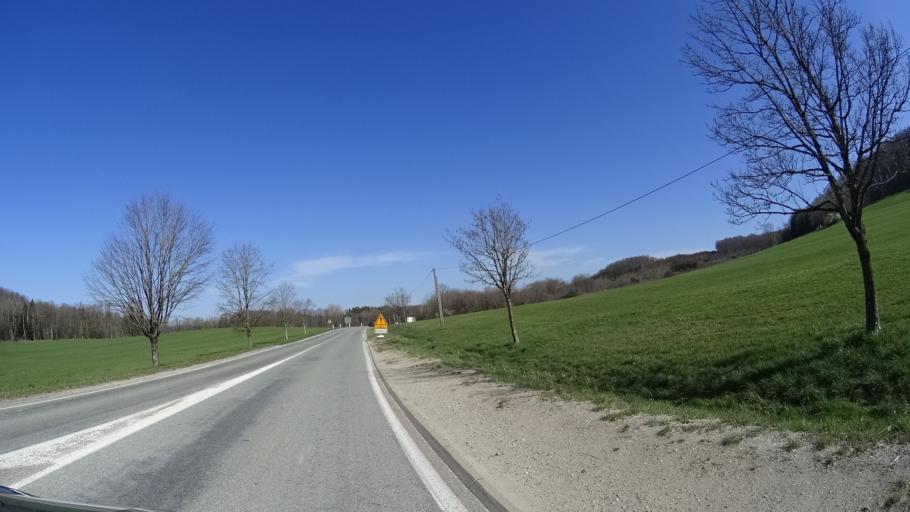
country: FR
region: Franche-Comte
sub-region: Departement du Doubs
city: Mamirolle
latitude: 47.1615
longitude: 6.1119
